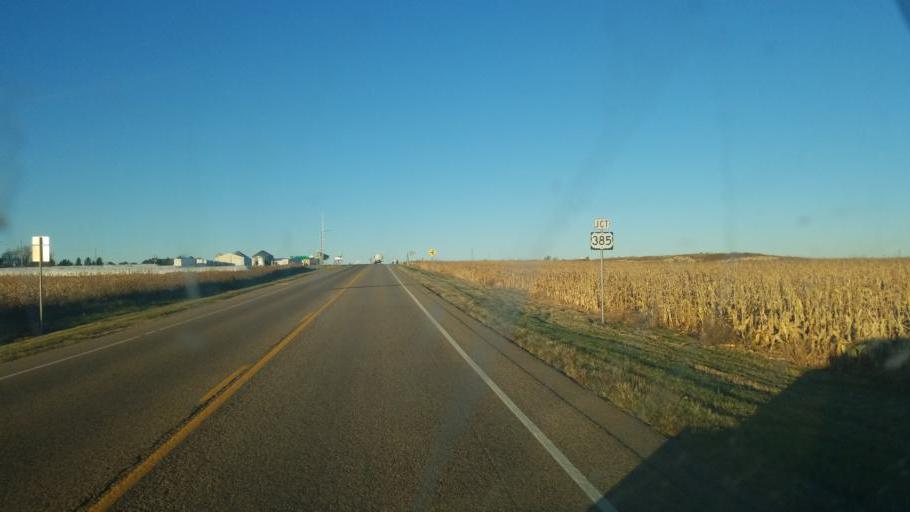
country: US
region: Colorado
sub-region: Cheyenne County
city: Cheyenne Wells
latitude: 38.8230
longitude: -102.3302
